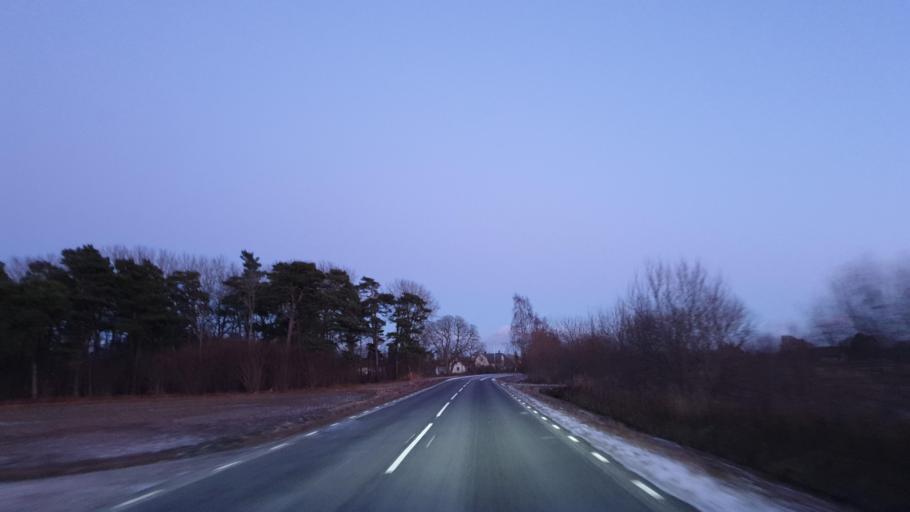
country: SE
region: Gotland
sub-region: Gotland
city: Slite
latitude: 57.4198
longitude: 18.8653
